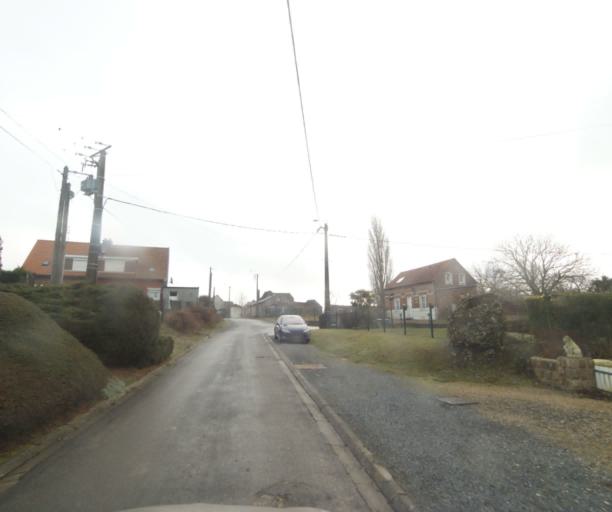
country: FR
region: Nord-Pas-de-Calais
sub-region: Departement du Nord
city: Famars
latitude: 50.2907
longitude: 3.5115
